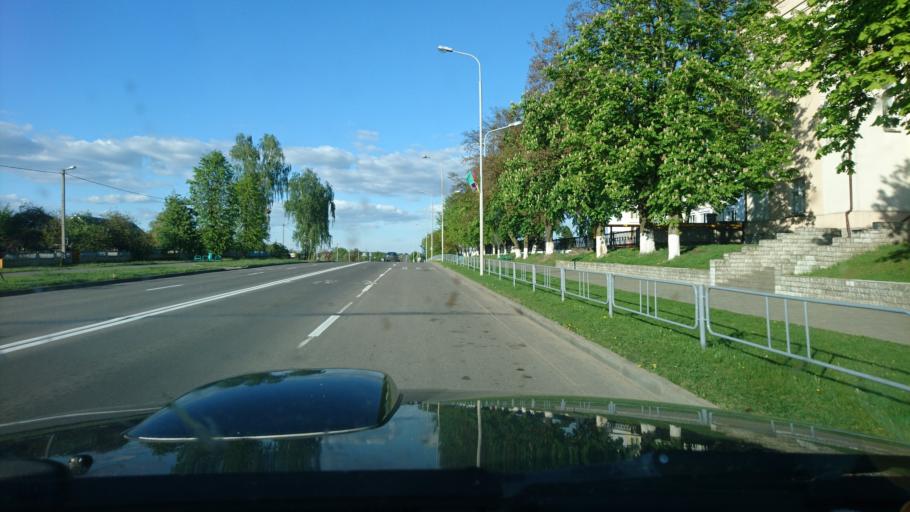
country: BY
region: Brest
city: Ivatsevichy
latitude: 52.7150
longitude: 25.3497
